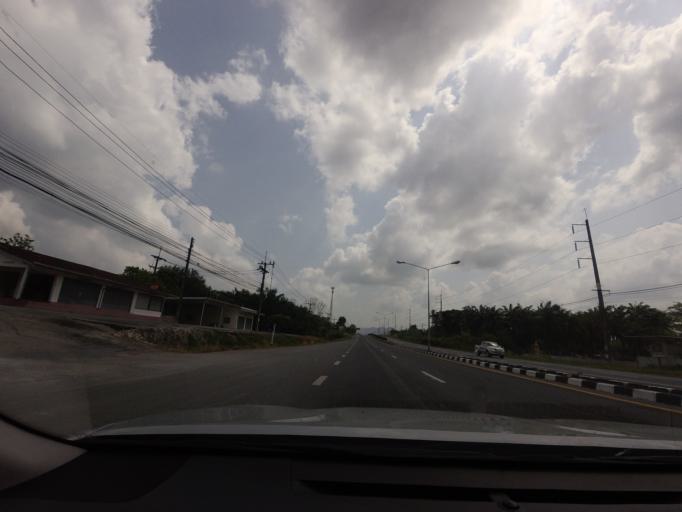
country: TH
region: Phangnga
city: Thap Put
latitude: 8.5074
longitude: 98.6764
